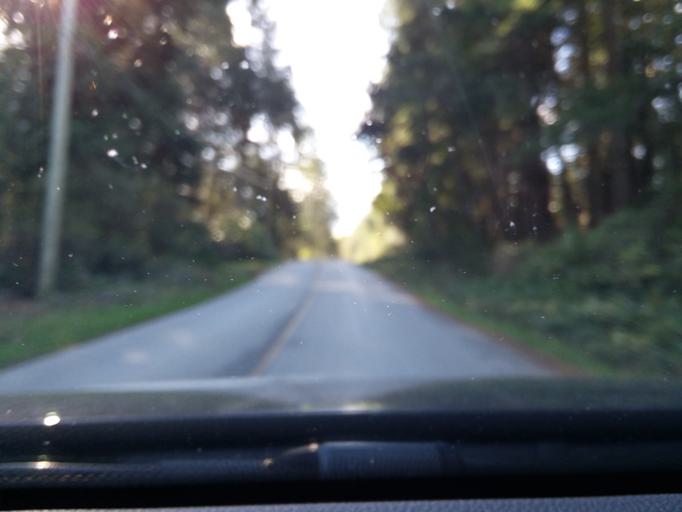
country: CA
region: British Columbia
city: North Cowichan
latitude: 48.9701
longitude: -123.5580
